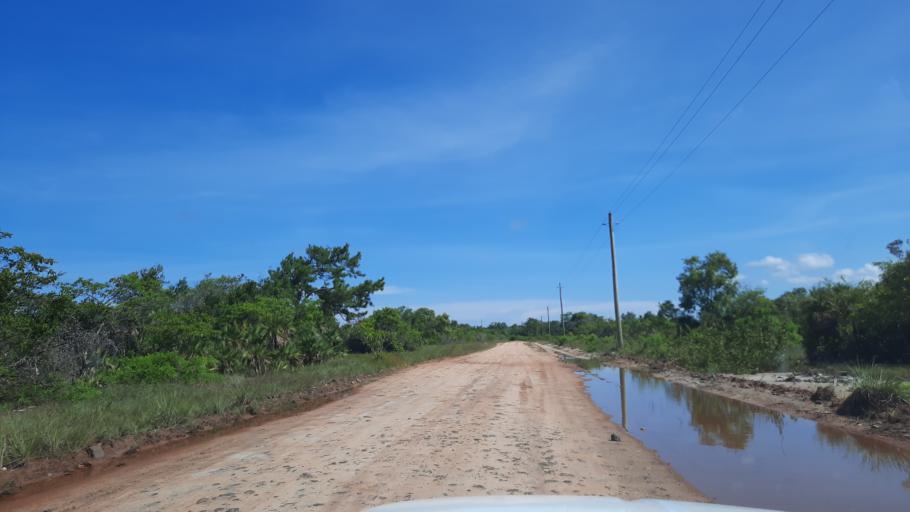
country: BZ
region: Stann Creek
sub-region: Dangriga
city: Dangriga
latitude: 17.1688
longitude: -88.3298
